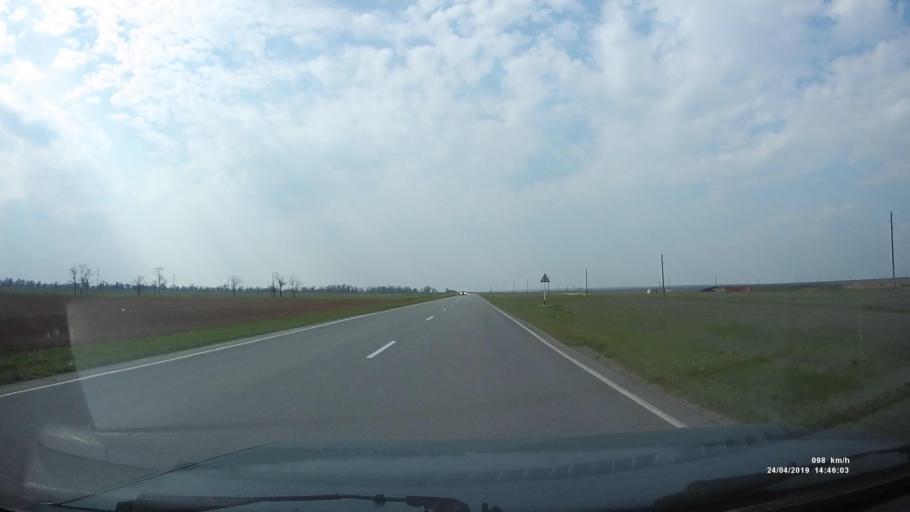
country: RU
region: Rostov
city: Remontnoye
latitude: 46.4783
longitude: 43.7967
